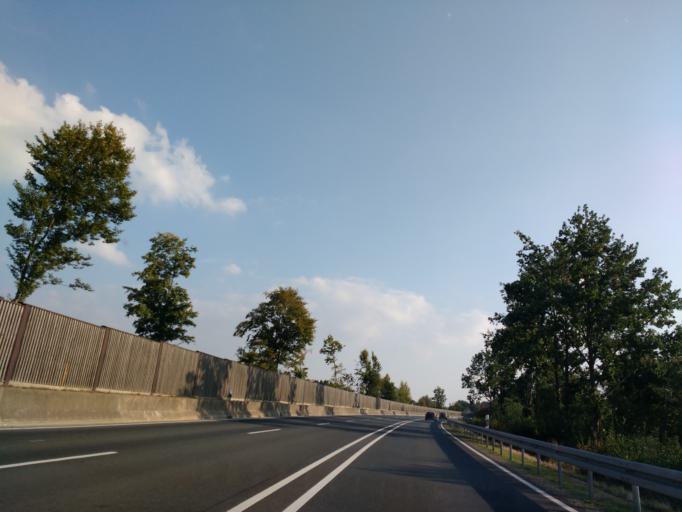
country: DE
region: North Rhine-Westphalia
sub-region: Regierungsbezirk Detmold
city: Steinheim
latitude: 51.8705
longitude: 9.1066
